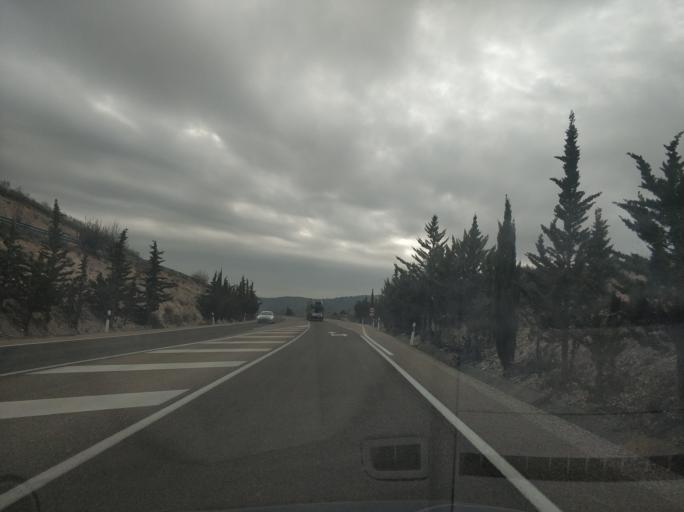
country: ES
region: Castille and Leon
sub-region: Provincia de Soria
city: Langa de Duero
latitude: 41.6215
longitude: -3.4539
